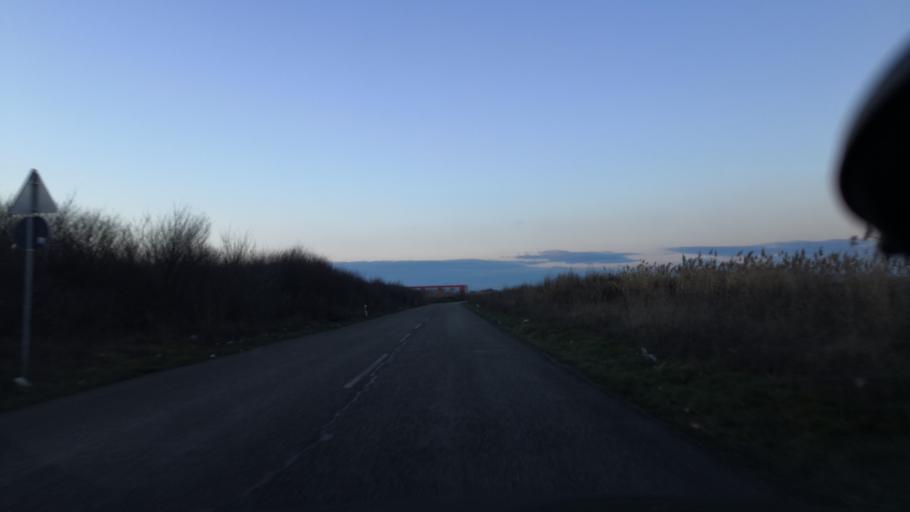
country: RS
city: Simanovci
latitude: 44.8805
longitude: 20.1191
